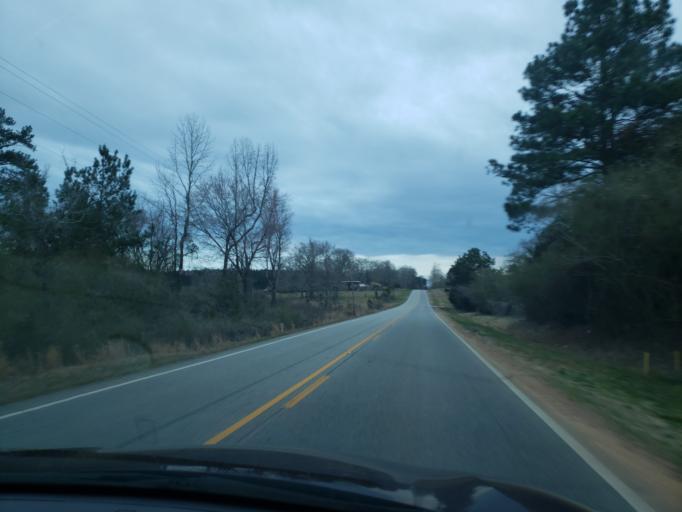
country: US
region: Alabama
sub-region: Chambers County
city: Lafayette
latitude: 32.9760
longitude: -85.4032
